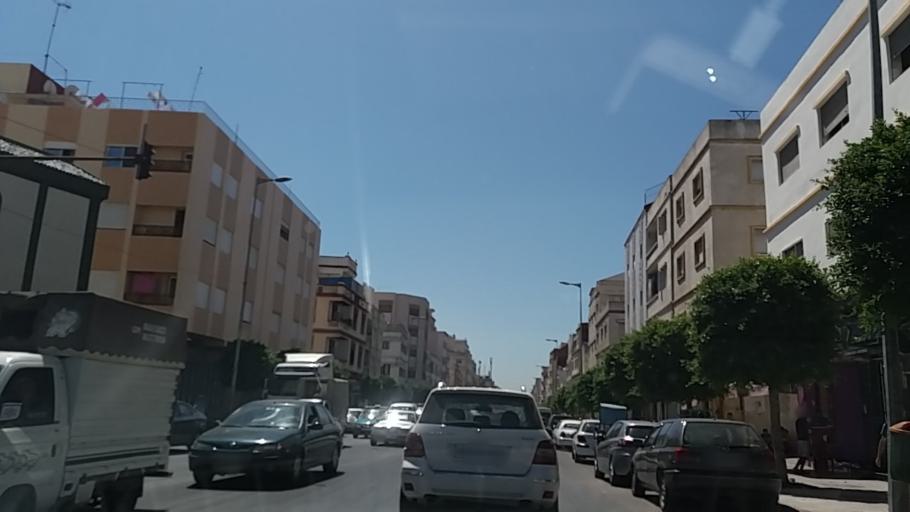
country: MA
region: Tanger-Tetouan
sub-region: Tanger-Assilah
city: Tangier
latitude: 35.7643
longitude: -5.8043
